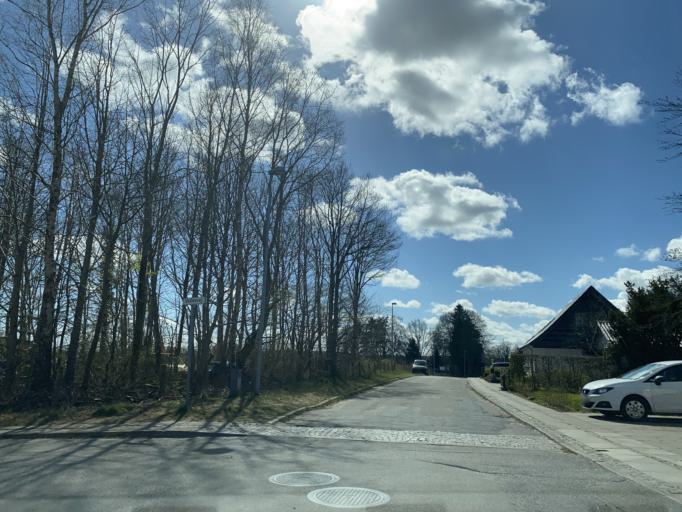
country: DK
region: Central Jutland
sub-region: Randers Kommune
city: Langa
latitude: 56.3862
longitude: 9.8902
